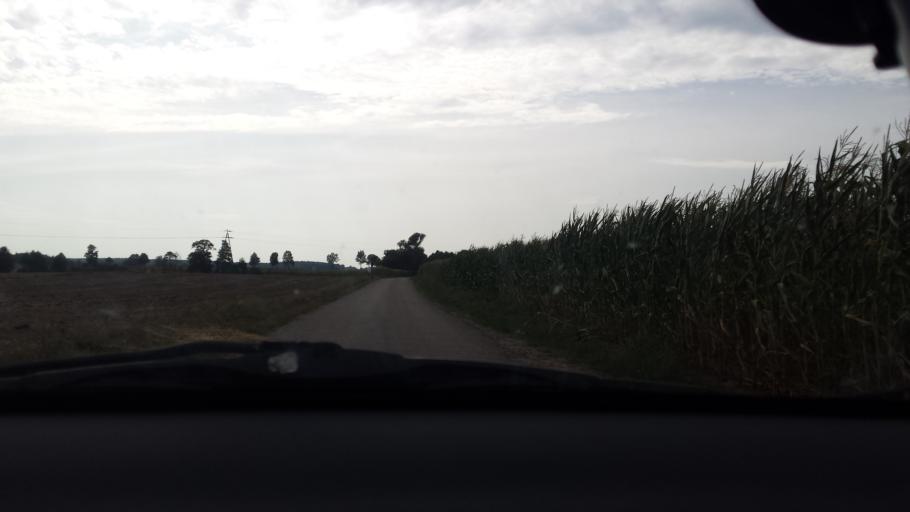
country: PL
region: Masovian Voivodeship
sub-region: Powiat makowski
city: Sypniewo
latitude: 52.9875
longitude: 21.3625
